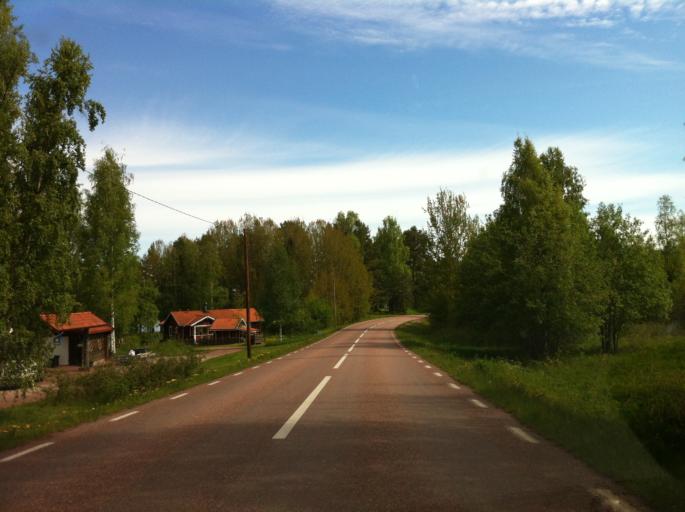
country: SE
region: Dalarna
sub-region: Mora Kommun
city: Mora
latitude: 60.8920
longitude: 14.5488
